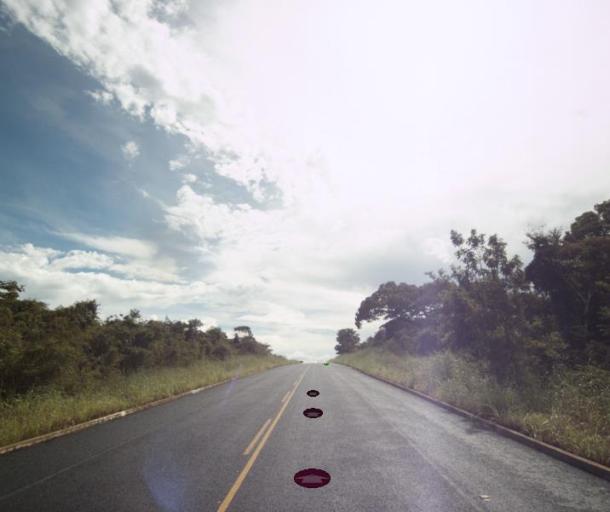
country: BR
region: Goias
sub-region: Sao Miguel Do Araguaia
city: Sao Miguel do Araguaia
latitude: -13.2981
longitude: -50.3297
